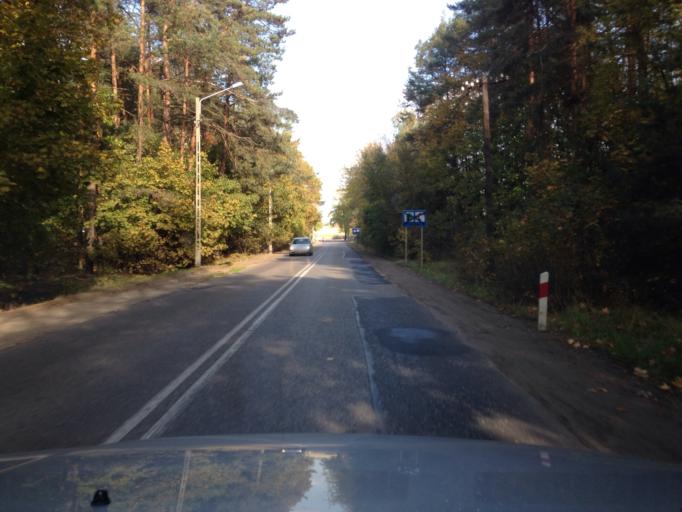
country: PL
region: Pomeranian Voivodeship
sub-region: Powiat starogardzki
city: Skorcz
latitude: 53.7892
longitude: 18.5082
